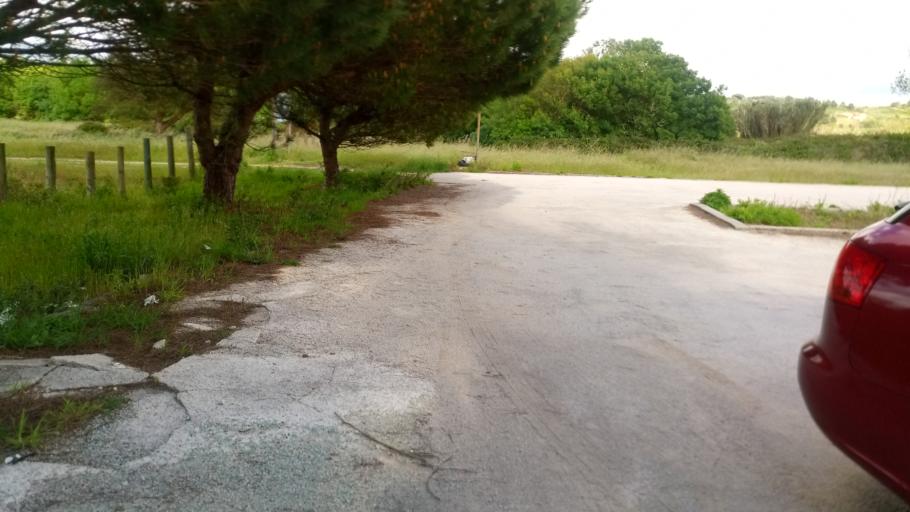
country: PT
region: Leiria
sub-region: Obidos
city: Obidos
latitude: 39.3904
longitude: -9.2009
